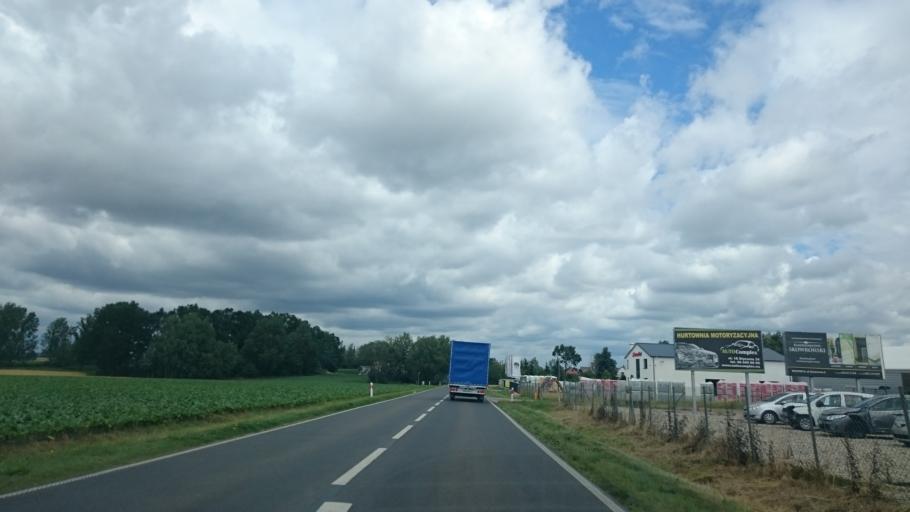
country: PL
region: Kujawsko-Pomorskie
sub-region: Powiat brodnicki
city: Brodnica
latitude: 53.2106
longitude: 19.3849
